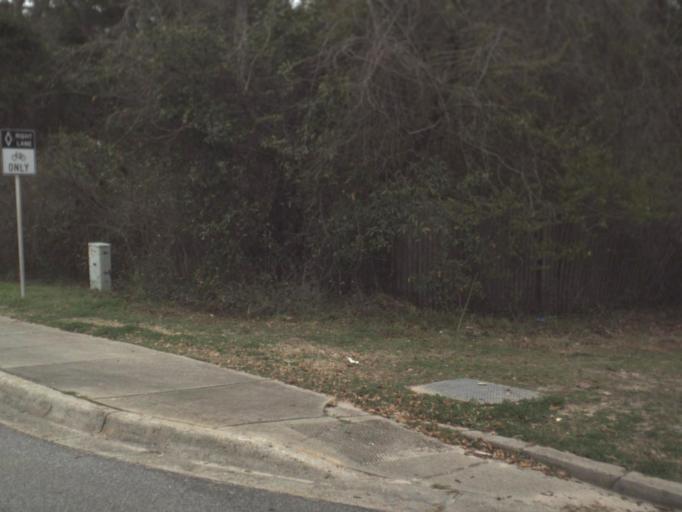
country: US
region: Florida
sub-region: Leon County
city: Tallahassee
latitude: 30.5476
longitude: -84.2253
